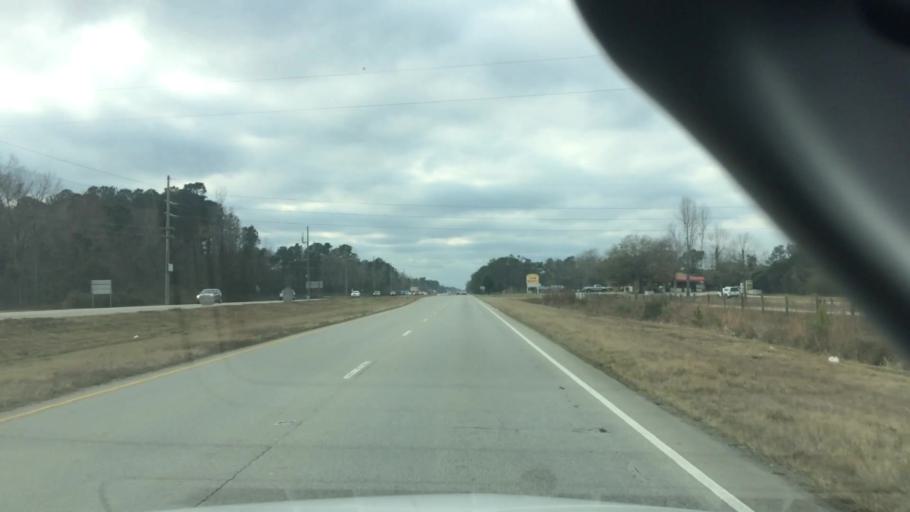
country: US
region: North Carolina
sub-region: Brunswick County
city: Shallotte
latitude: 33.9547
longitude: -78.4491
